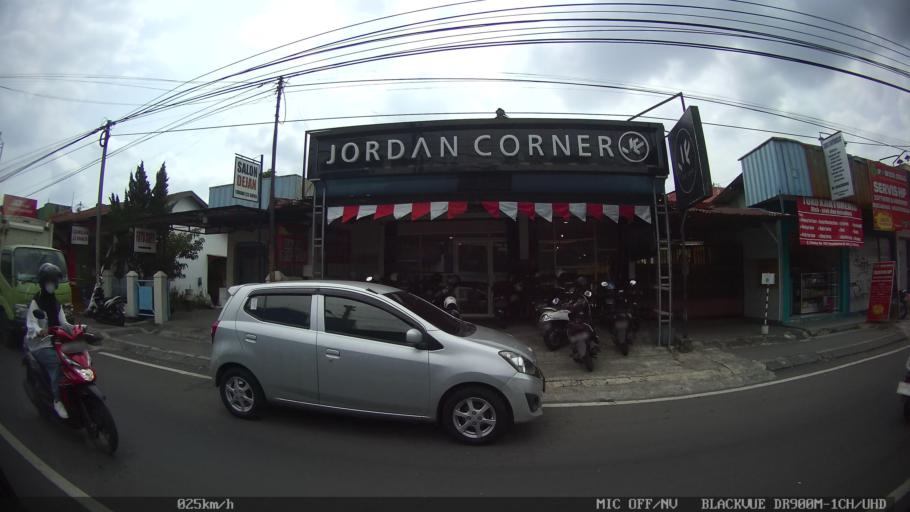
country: ID
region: Daerah Istimewa Yogyakarta
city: Yogyakarta
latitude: -7.7881
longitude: 110.3941
